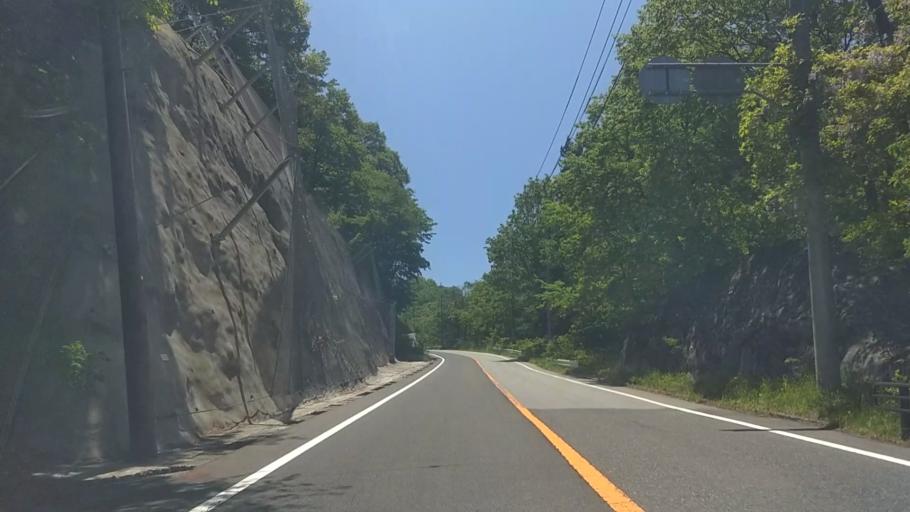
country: JP
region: Yamanashi
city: Nirasaki
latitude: 35.8831
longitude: 138.4287
